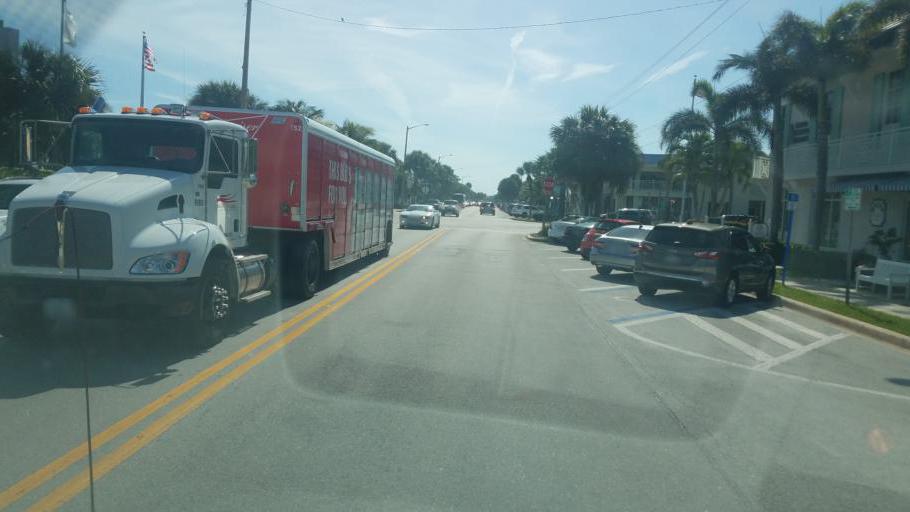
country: US
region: Florida
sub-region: Indian River County
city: Vero Beach
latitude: 27.6539
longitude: -80.3567
